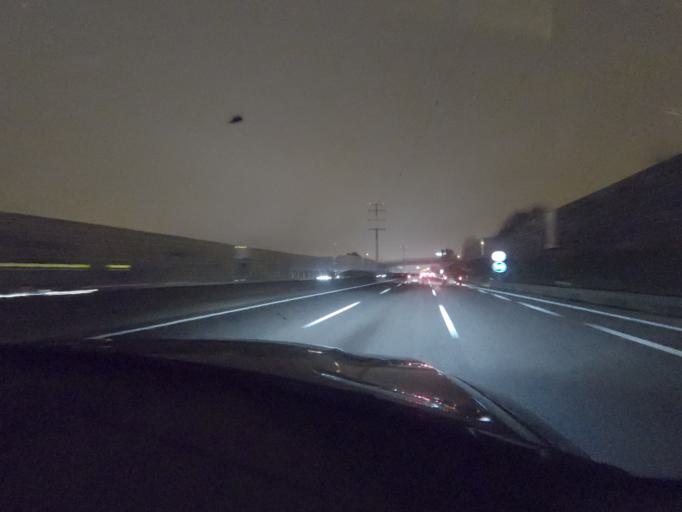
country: PT
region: Lisbon
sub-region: Loures
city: Sao Joao da Talha
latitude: 38.8204
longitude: -9.1000
